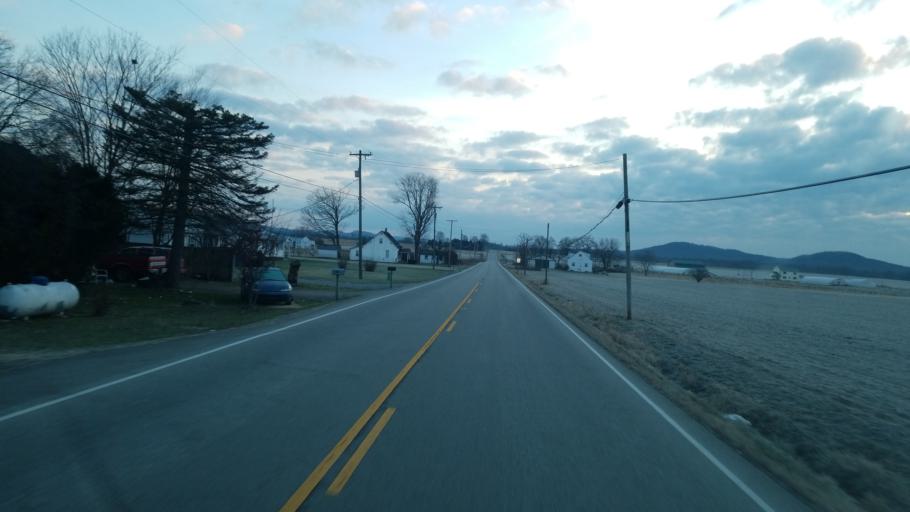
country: US
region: Ohio
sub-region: Highland County
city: Greenfield
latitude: 39.2203
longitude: -83.4176
